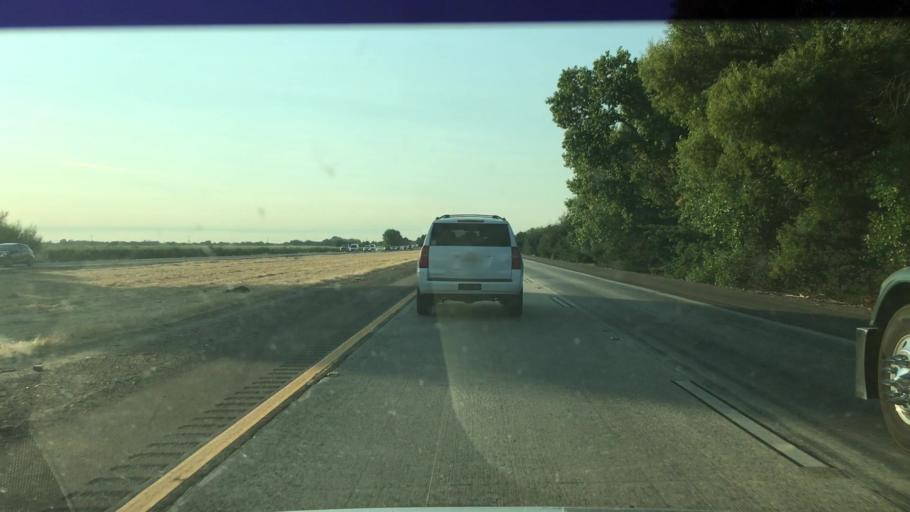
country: US
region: California
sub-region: San Joaquin County
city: Thornton
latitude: 38.2398
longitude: -121.4404
